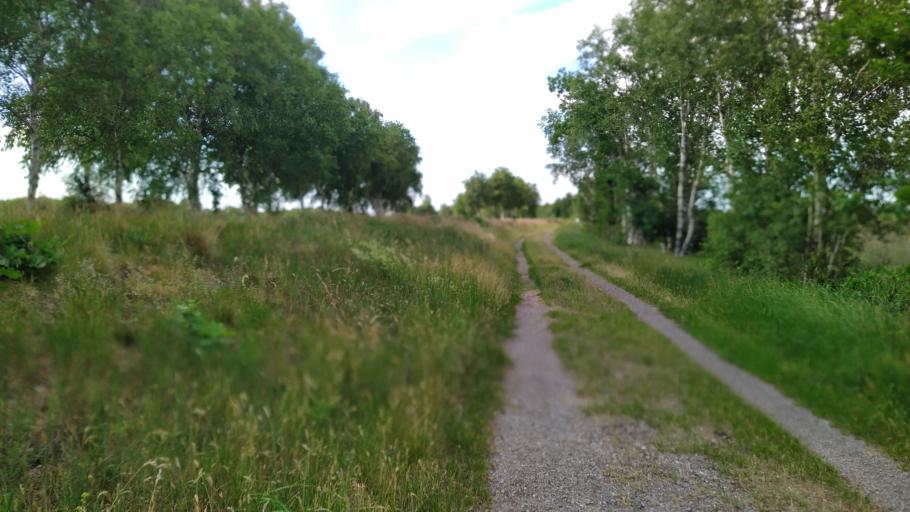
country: DE
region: Lower Saxony
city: Stinstedt
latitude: 53.6449
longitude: 8.9494
